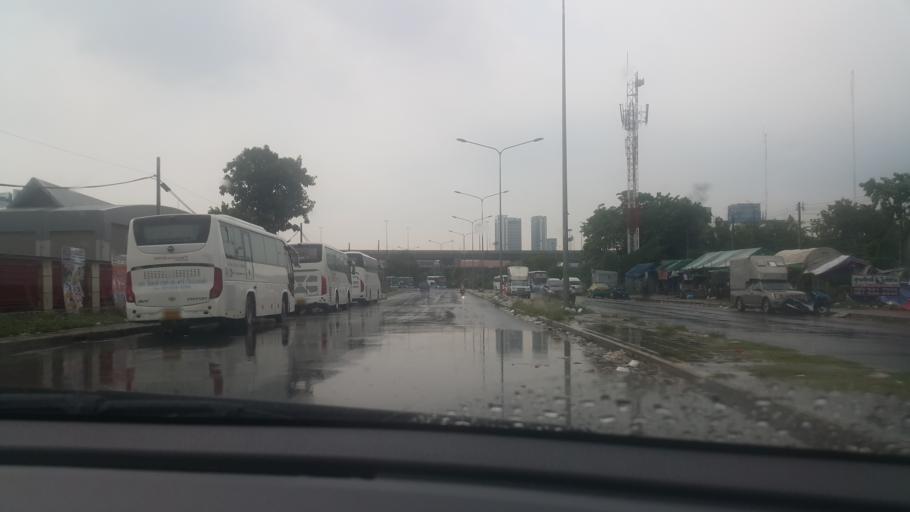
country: TH
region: Bangkok
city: Bang Sue
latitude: 13.8150
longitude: 100.5465
